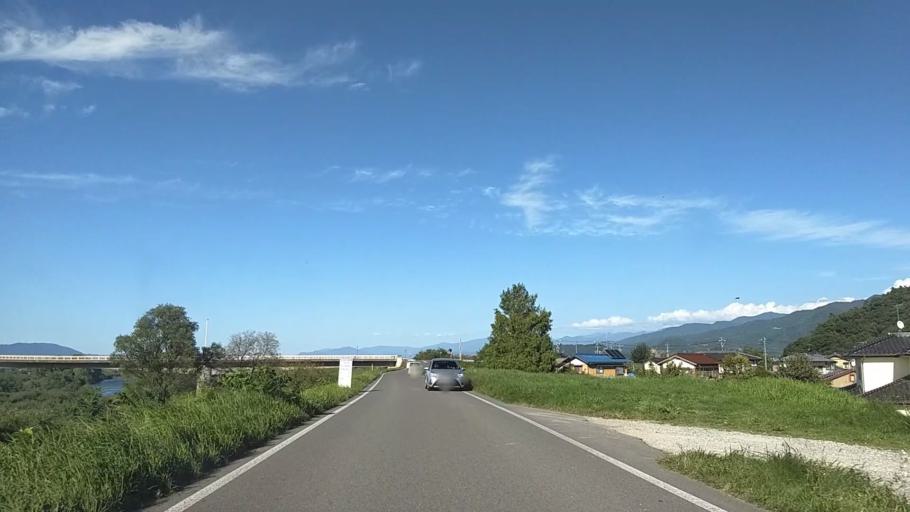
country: JP
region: Nagano
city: Nagano-shi
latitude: 36.5600
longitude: 138.1575
